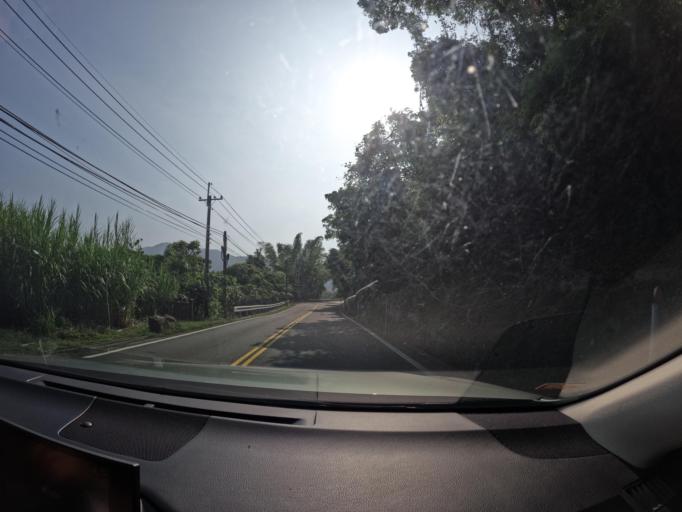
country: TW
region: Taiwan
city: Yujing
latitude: 23.0764
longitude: 120.5376
